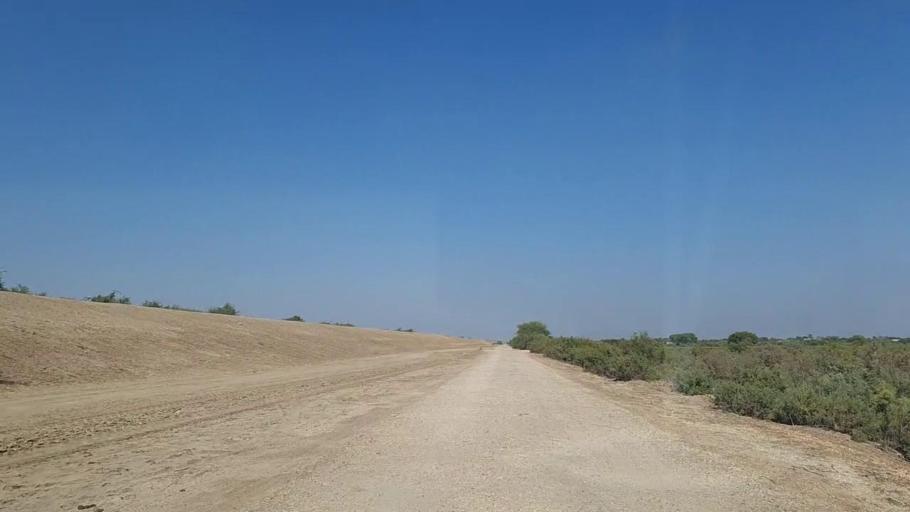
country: PK
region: Sindh
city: Chuhar Jamali
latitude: 24.4613
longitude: 68.0027
